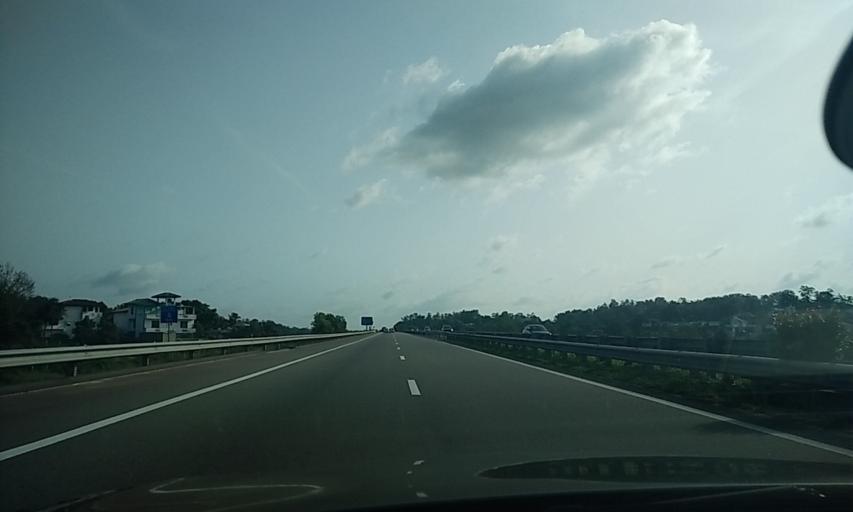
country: LK
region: Western
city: Homagama
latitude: 6.8913
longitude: 79.9776
